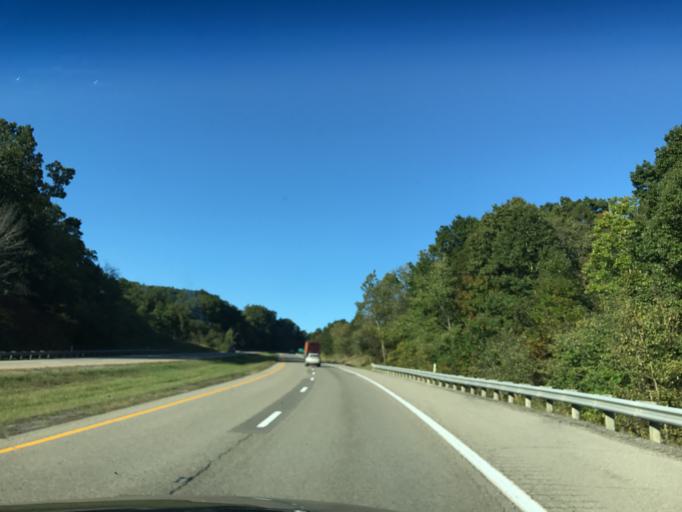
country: US
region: Ohio
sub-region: Washington County
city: Newport
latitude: 39.2528
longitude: -81.2522
